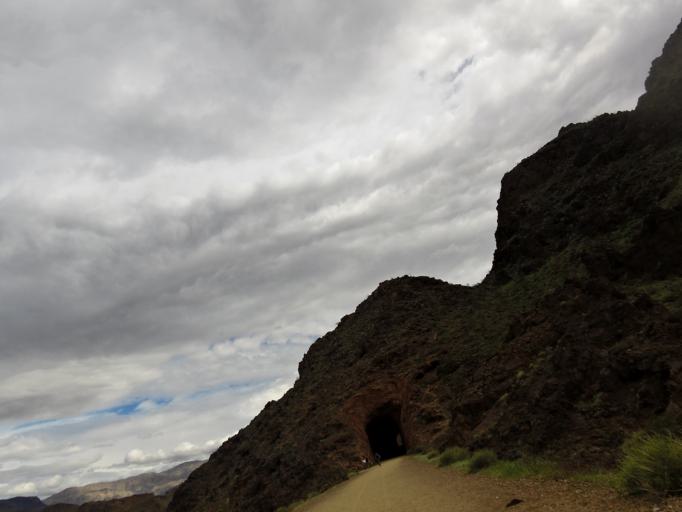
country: US
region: Nevada
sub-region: Clark County
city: Boulder City
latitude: 36.0173
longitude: -114.7746
